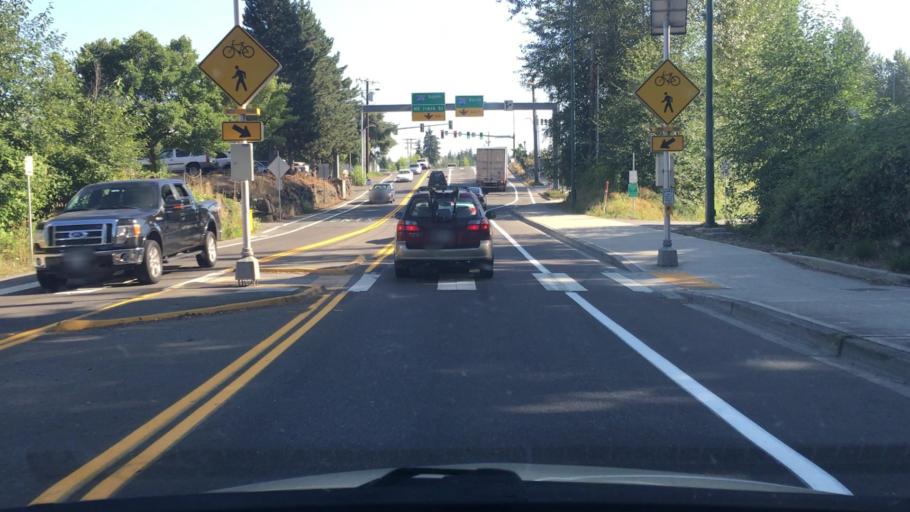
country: US
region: Washington
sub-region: King County
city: Kingsgate
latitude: 47.7054
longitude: -122.1812
